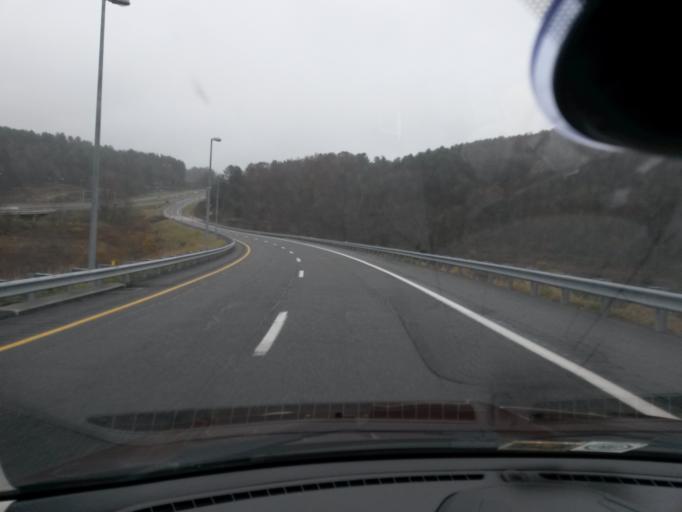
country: US
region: Virginia
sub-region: Carroll County
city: Hillsville
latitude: 36.7520
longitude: -80.7538
